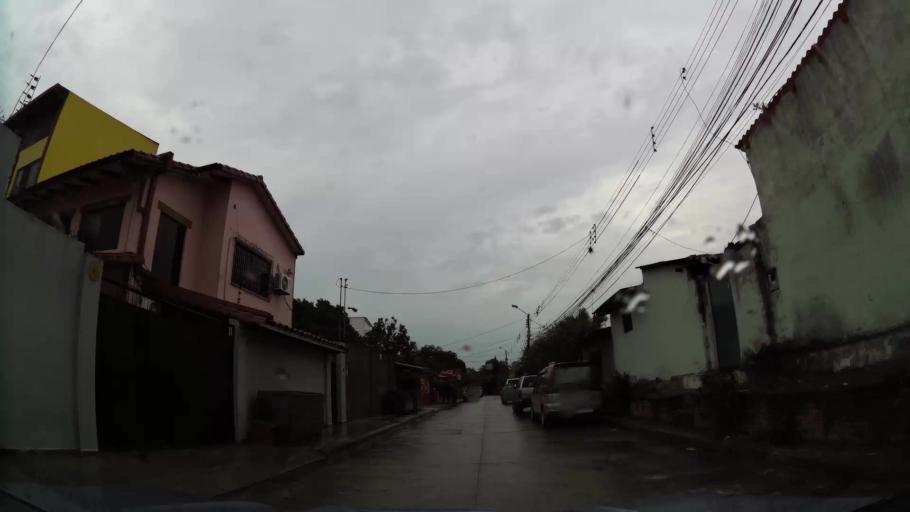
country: BO
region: Santa Cruz
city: Santa Cruz de la Sierra
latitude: -17.7902
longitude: -63.2164
